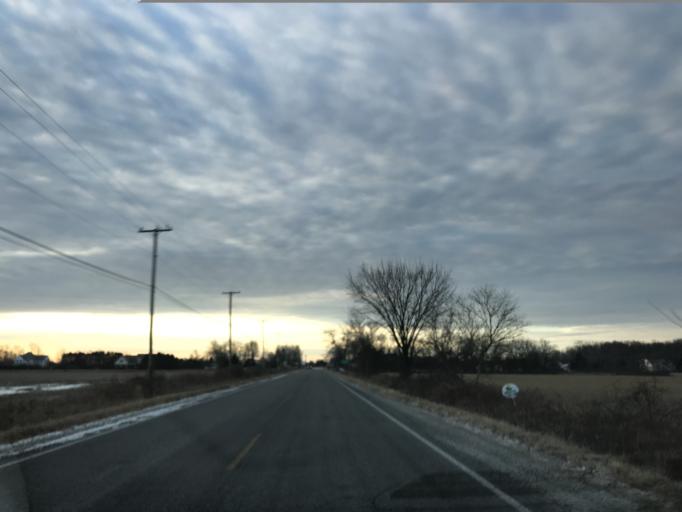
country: US
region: Michigan
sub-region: Macomb County
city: Armada
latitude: 42.8978
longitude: -82.8829
